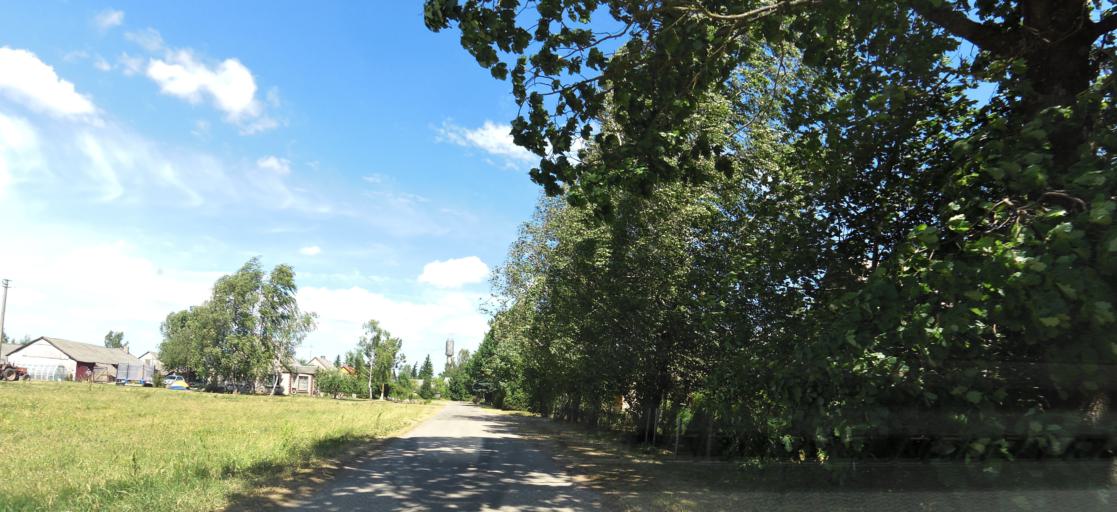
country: LT
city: Kupiskis
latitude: 55.9707
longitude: 24.9956
